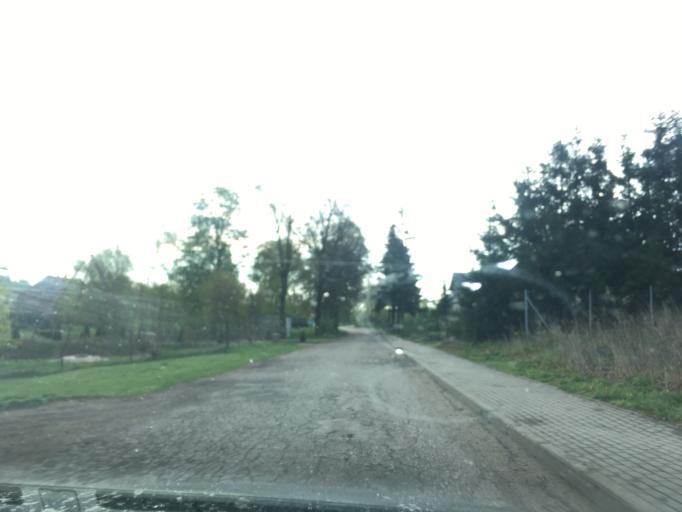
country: PL
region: Warmian-Masurian Voivodeship
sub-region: Powiat ostrodzki
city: Dabrowno
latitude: 53.4374
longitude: 19.9842
